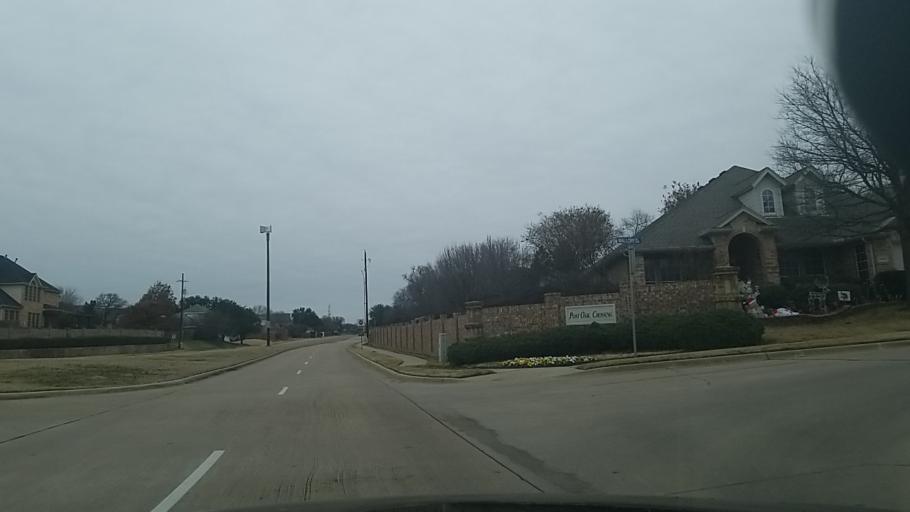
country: US
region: Texas
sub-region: Denton County
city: Corinth
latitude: 33.1348
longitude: -97.0738
